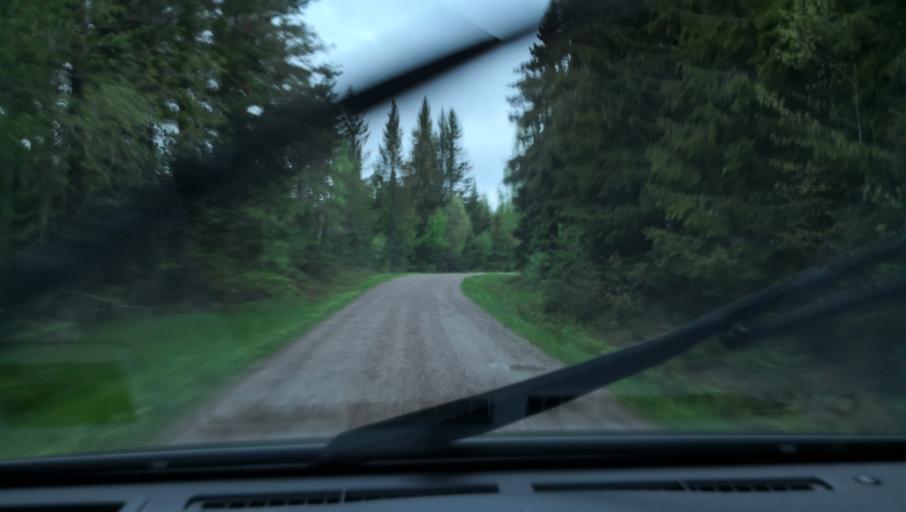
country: SE
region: Uppsala
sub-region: Heby Kommun
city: OEstervala
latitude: 59.9873
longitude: 17.2592
